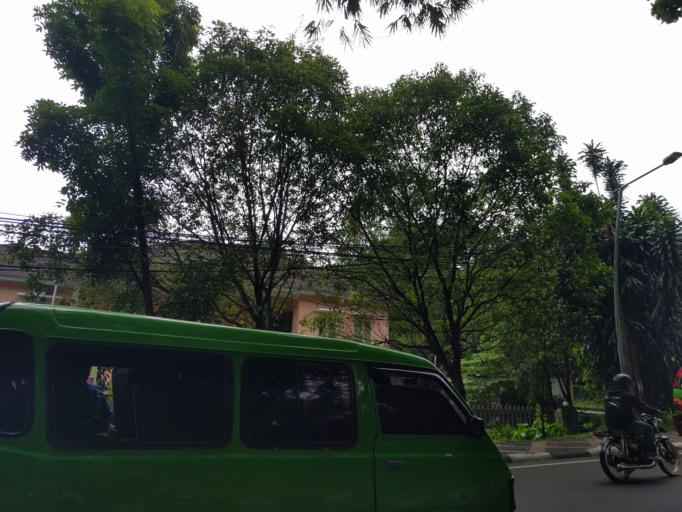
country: ID
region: West Java
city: Bogor
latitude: -6.5934
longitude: 106.8027
